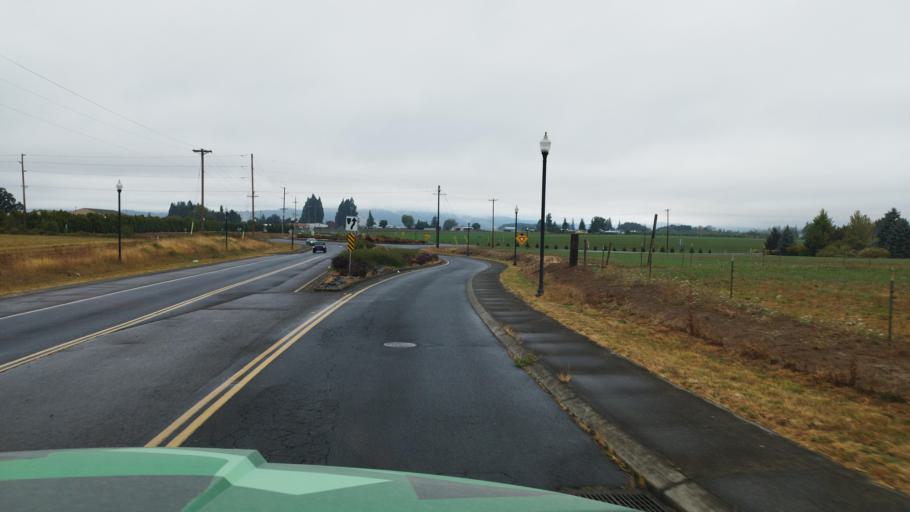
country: US
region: Oregon
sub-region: Washington County
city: Cornelius
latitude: 45.5514
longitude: -123.0710
